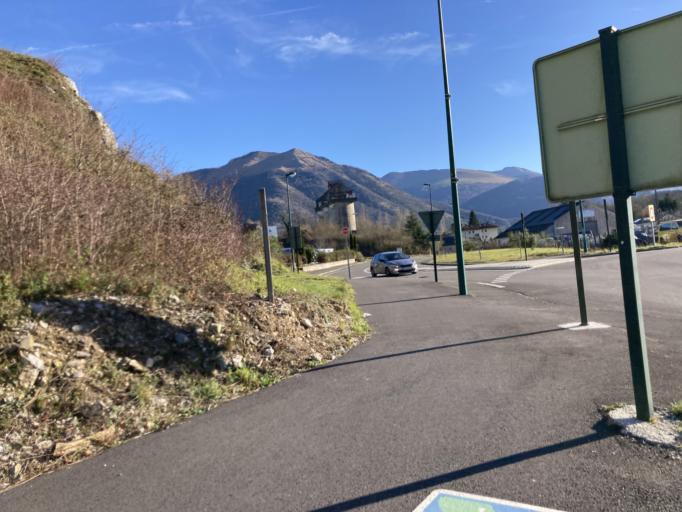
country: FR
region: Aquitaine
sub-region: Departement des Pyrenees-Atlantiques
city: Arudy
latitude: 43.1010
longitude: -0.4335
